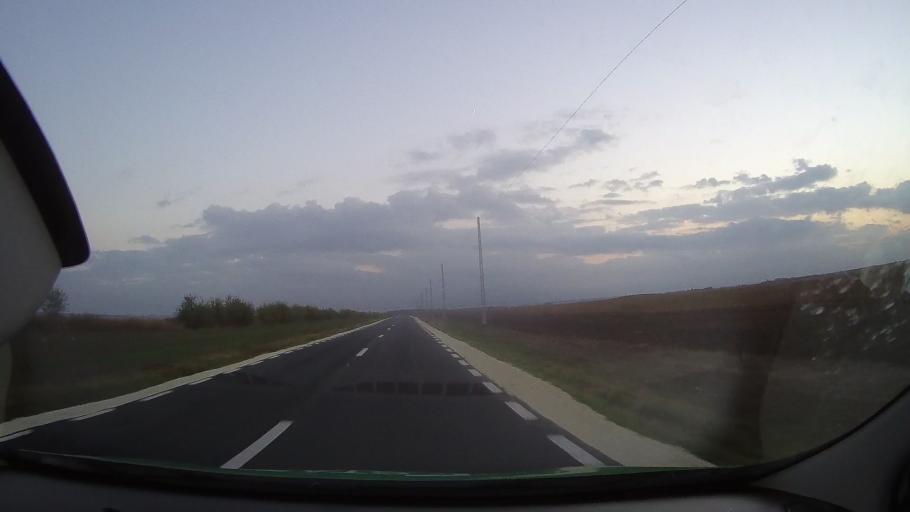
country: RO
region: Constanta
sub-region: Comuna Oltina
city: Oltina
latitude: 44.1271
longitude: 27.6683
